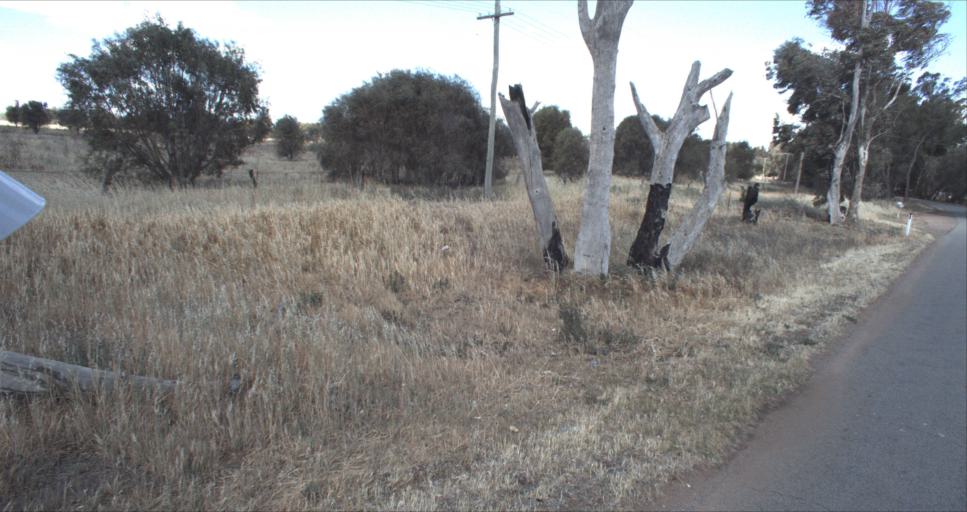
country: AU
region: New South Wales
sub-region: Leeton
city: Leeton
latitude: -34.5129
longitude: 146.2326
